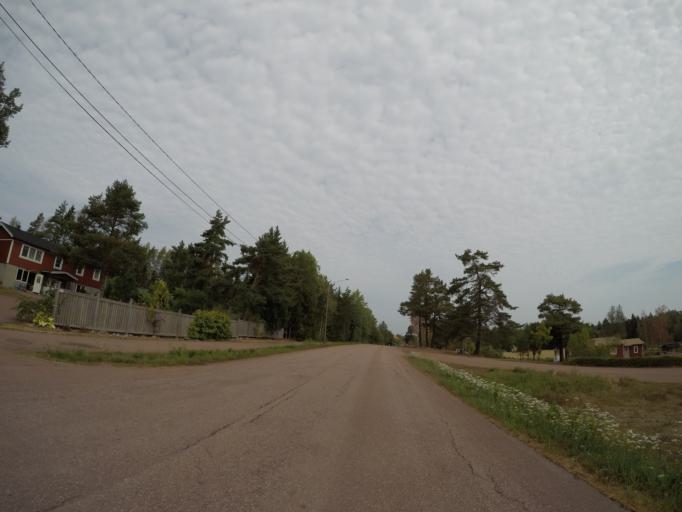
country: AX
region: Alands landsbygd
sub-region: Finstroem
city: Finstroem
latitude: 60.2215
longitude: 19.9806
